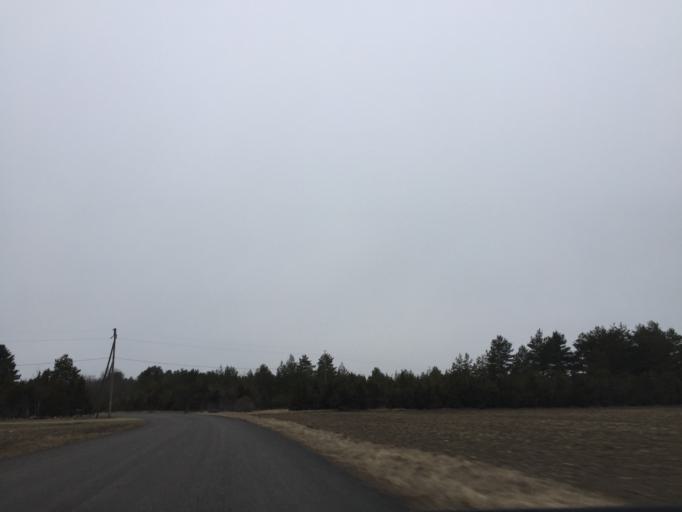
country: EE
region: Laeaene
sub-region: Lihula vald
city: Lihula
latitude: 58.6424
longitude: 23.6296
